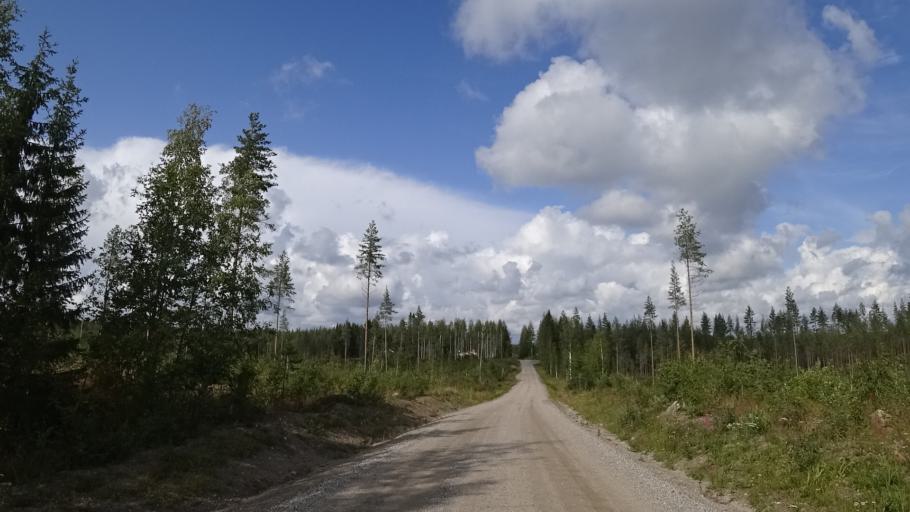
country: FI
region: North Karelia
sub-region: Pielisen Karjala
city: Lieksa
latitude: 63.5848
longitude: 30.1335
